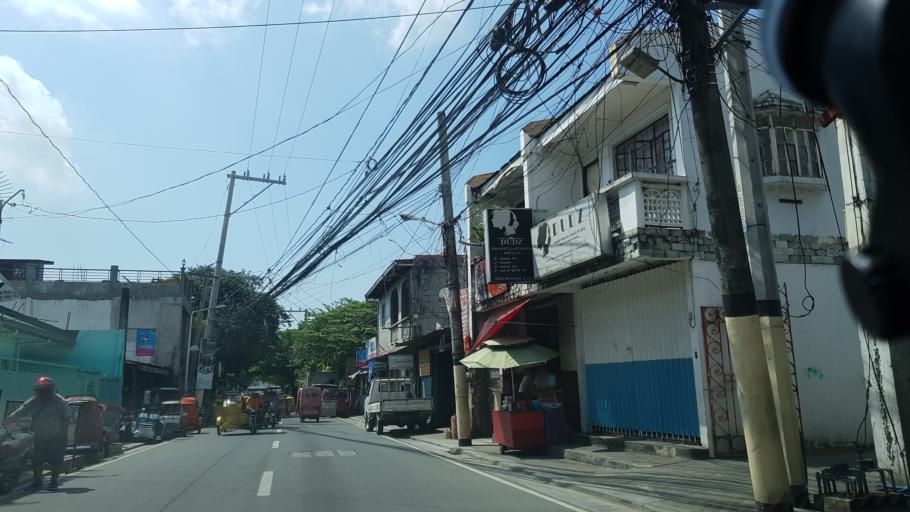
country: PH
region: Calabarzon
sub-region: Province of Rizal
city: Las Pinas
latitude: 14.4645
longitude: 120.9859
